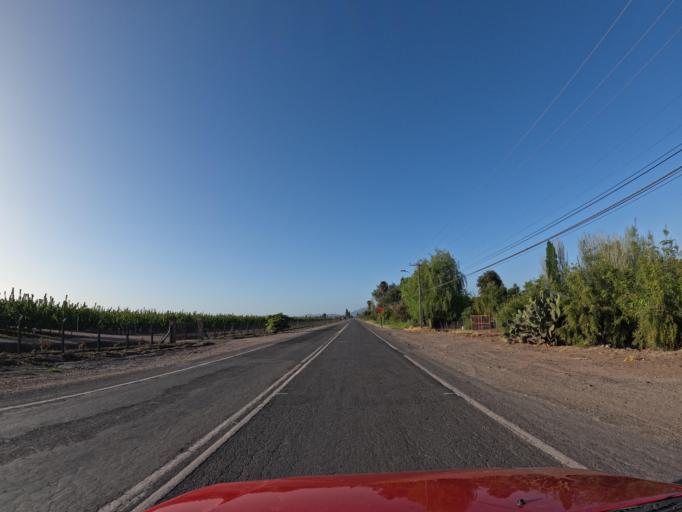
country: CL
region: O'Higgins
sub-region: Provincia de Colchagua
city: Santa Cruz
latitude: -34.5142
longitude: -71.3641
